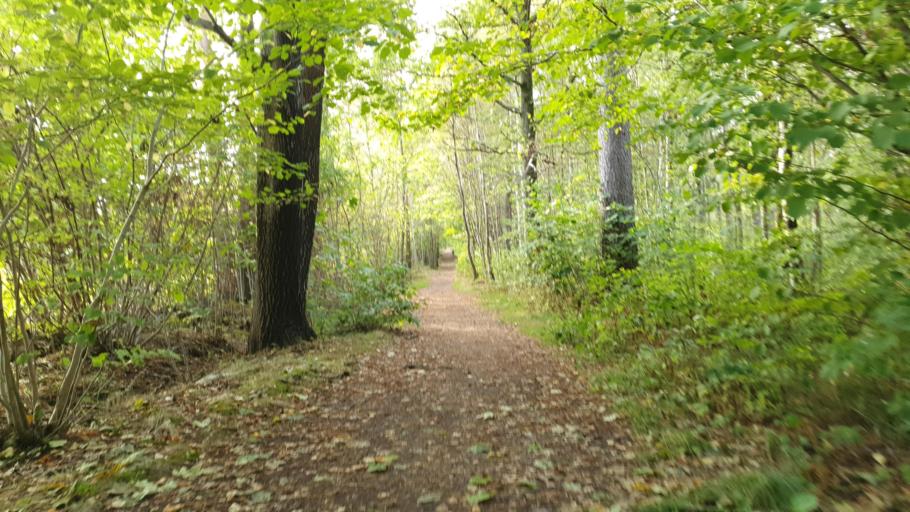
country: NO
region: Vestfold
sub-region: Tonsberg
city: Tonsberg
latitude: 59.2826
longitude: 10.4232
